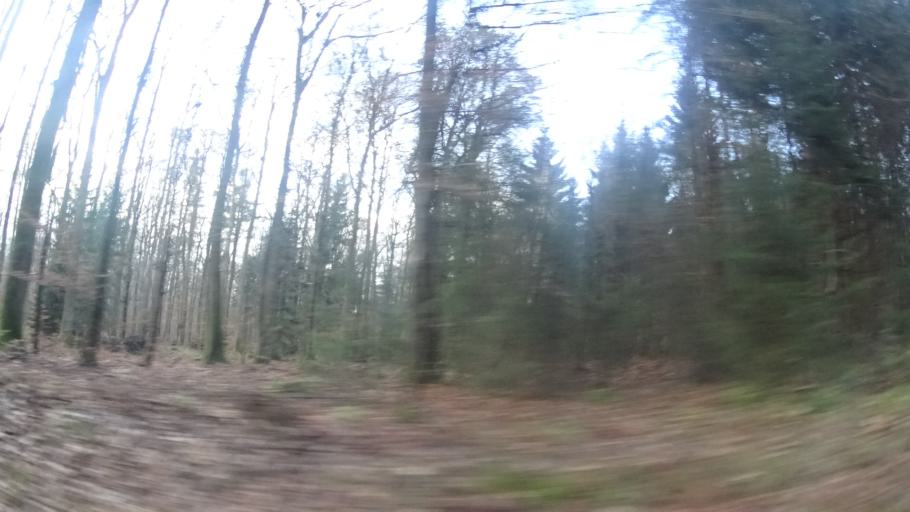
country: DE
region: Hesse
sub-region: Regierungsbezirk Kassel
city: Petersberg
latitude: 50.6103
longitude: 9.7577
